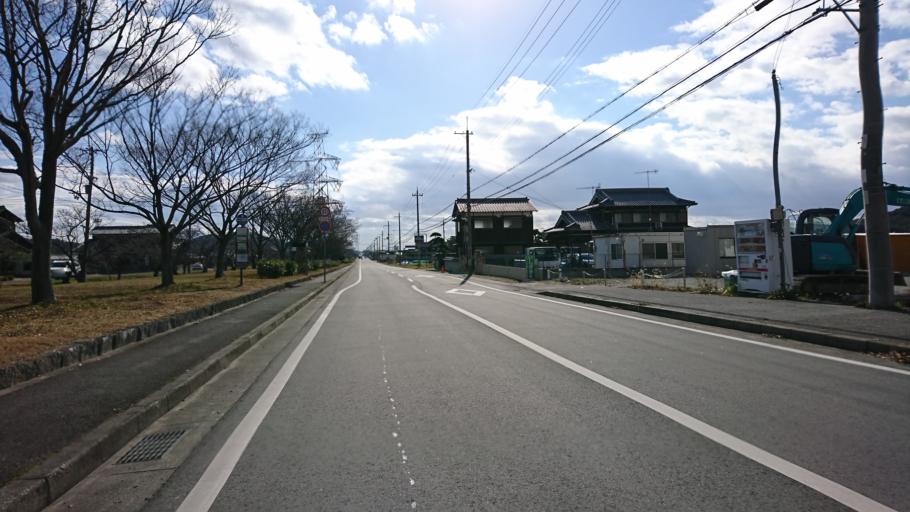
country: JP
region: Hyogo
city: Kakogawacho-honmachi
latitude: 34.8040
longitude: 134.7828
